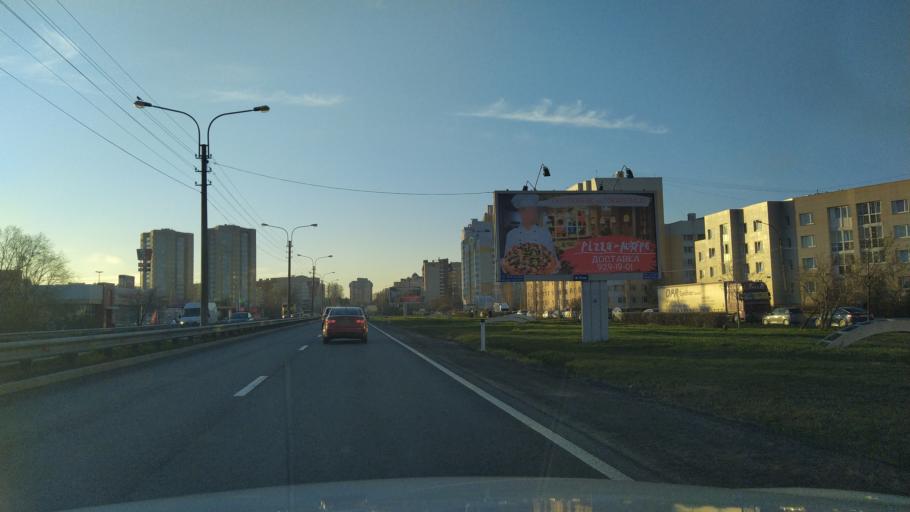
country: RU
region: St.-Petersburg
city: Razliv
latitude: 60.0814
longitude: 29.9594
